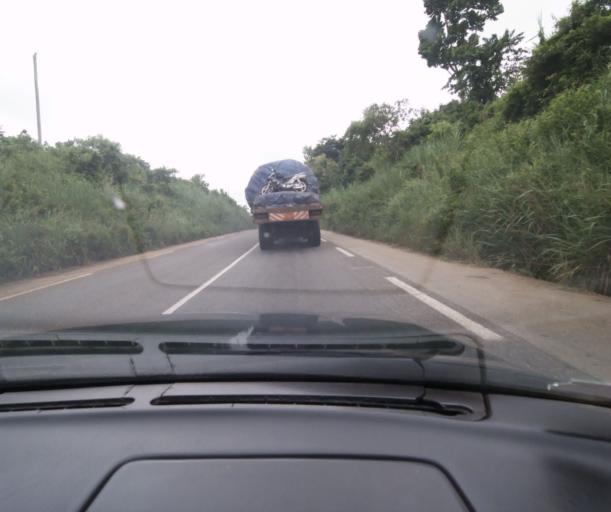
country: CM
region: Centre
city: Ombesa
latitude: 4.5723
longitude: 11.2665
